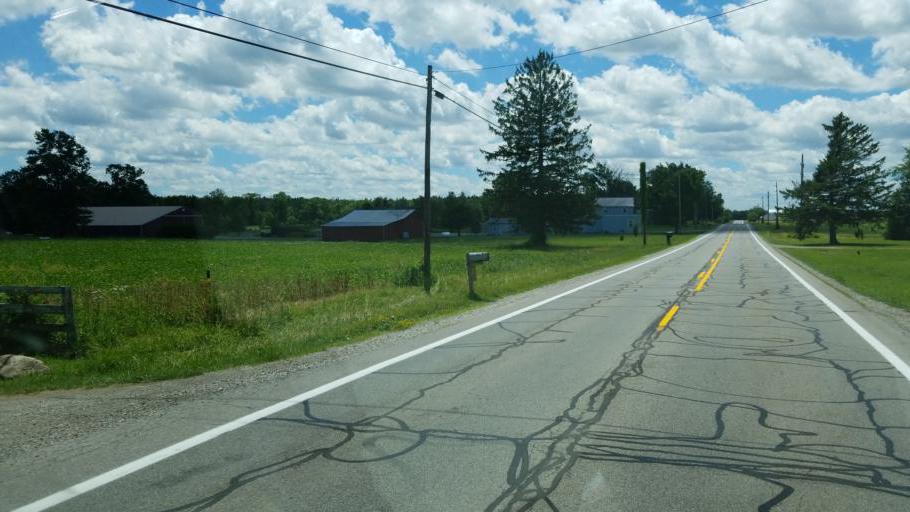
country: US
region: Ohio
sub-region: Morrow County
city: Mount Gilead
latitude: 40.5746
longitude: -82.8245
